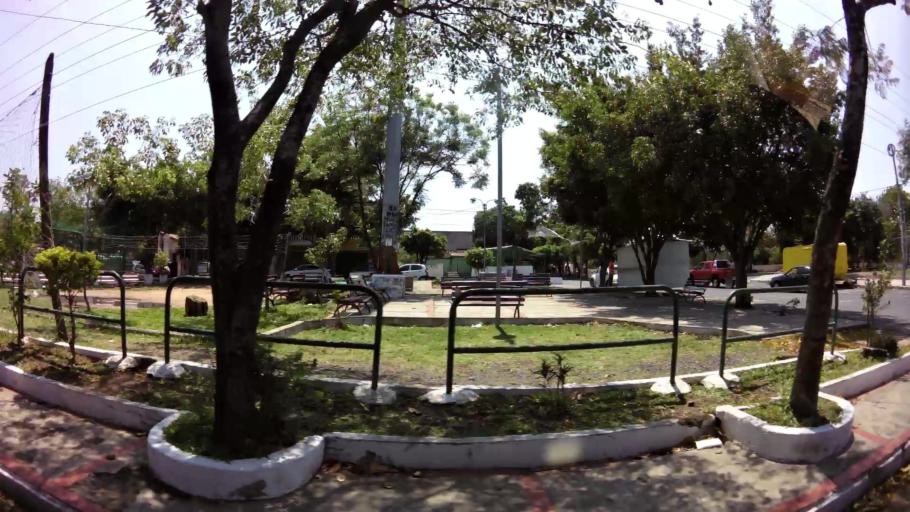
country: PY
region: Asuncion
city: Asuncion
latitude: -25.3039
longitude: -57.6501
